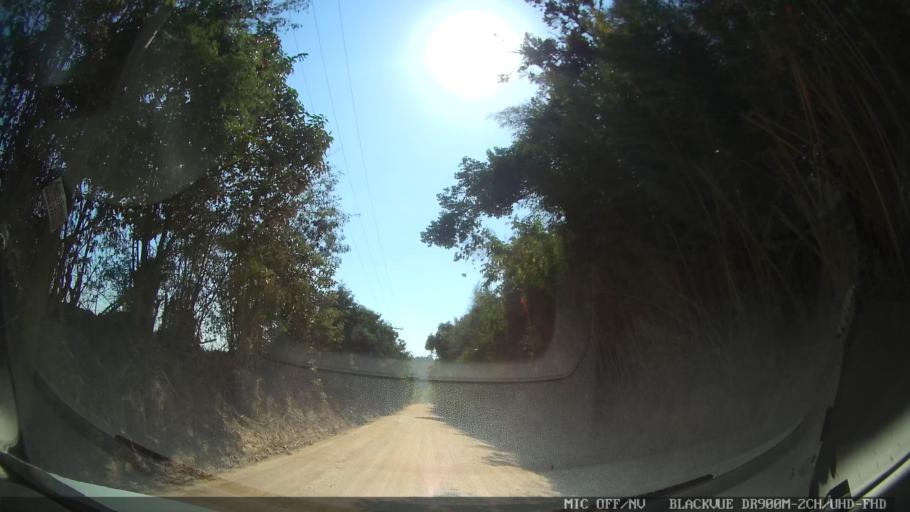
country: BR
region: Sao Paulo
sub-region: Itupeva
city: Itupeva
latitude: -23.1072
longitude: -47.0856
